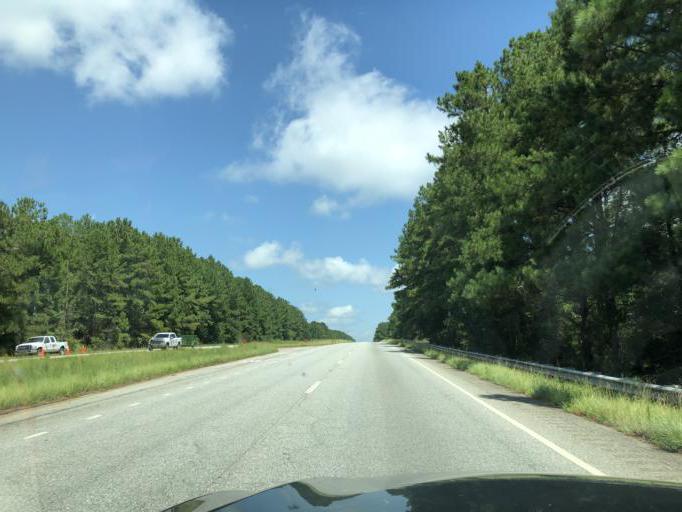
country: US
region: Alabama
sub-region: Henry County
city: Abbeville
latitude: 31.6754
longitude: -85.2793
